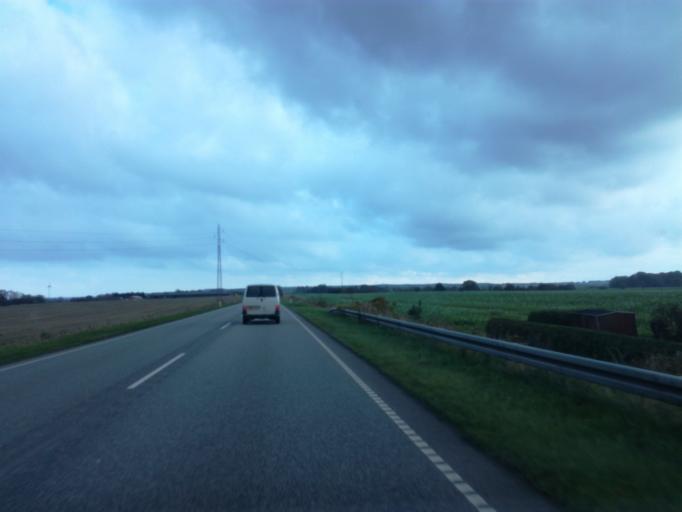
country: DK
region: South Denmark
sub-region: Vejle Kommune
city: Brejning
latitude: 55.6288
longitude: 9.7050
